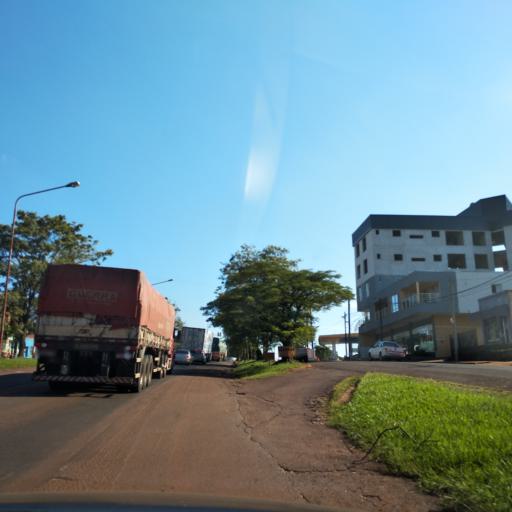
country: AR
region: Misiones
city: Jardin America
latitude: -27.0423
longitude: -55.2337
